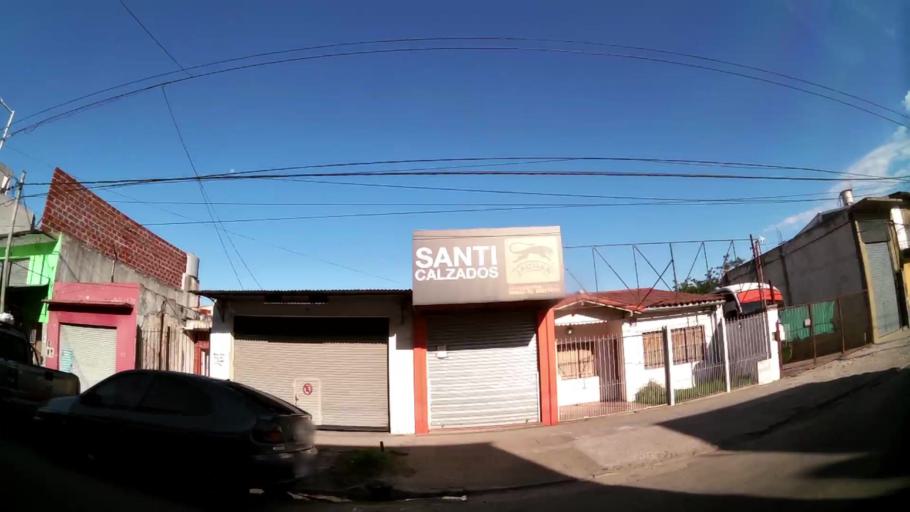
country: AR
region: Buenos Aires
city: Santa Catalina - Dique Lujan
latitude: -34.4932
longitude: -58.7276
